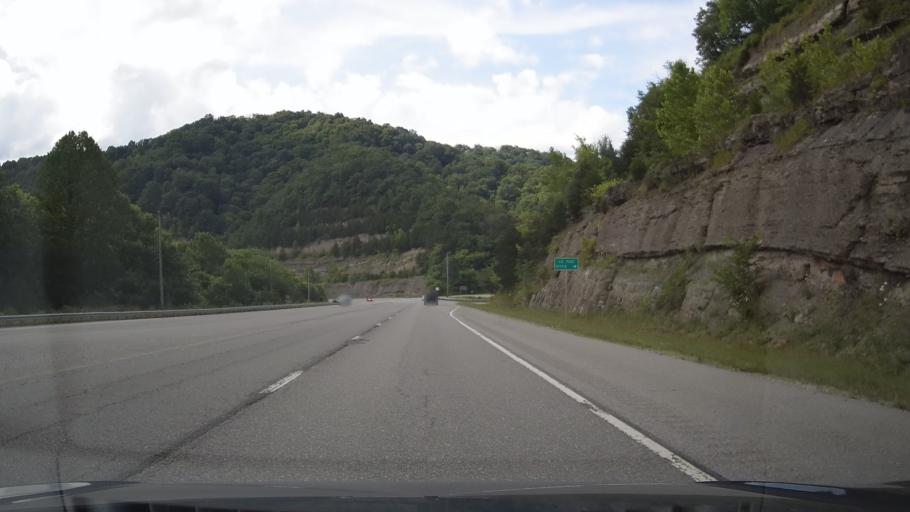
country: US
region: Kentucky
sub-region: Pike County
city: Coal Run Village
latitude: 37.5912
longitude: -82.6618
